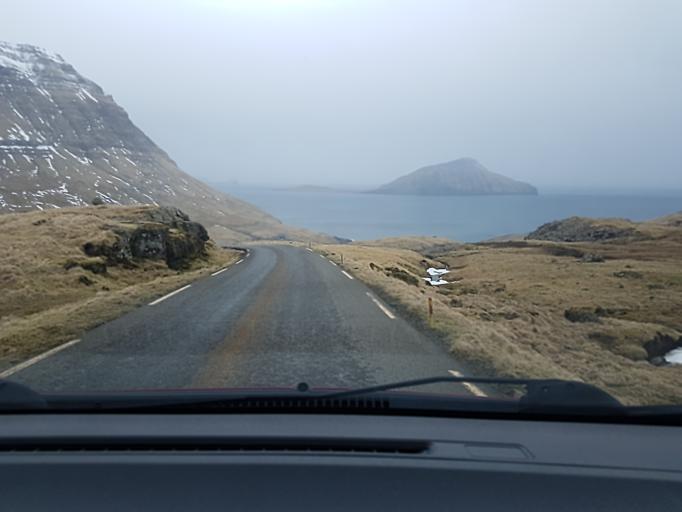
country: FO
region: Streymoy
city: Kollafjordhur
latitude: 62.0490
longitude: -6.9228
